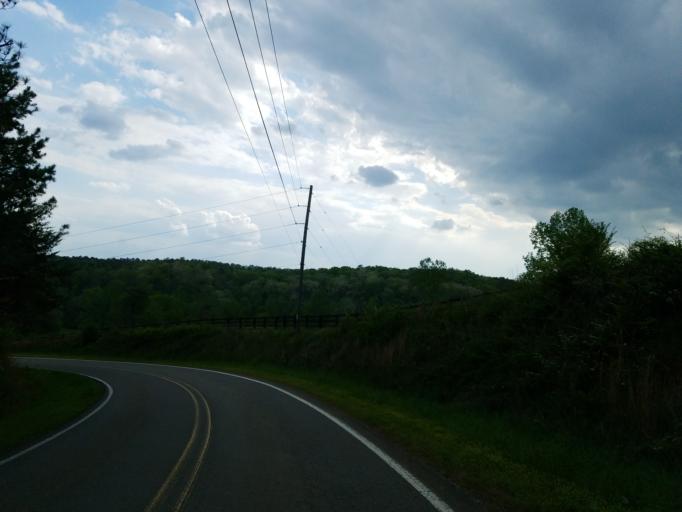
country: US
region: Georgia
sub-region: Pickens County
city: Jasper
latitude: 34.4385
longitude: -84.4526
